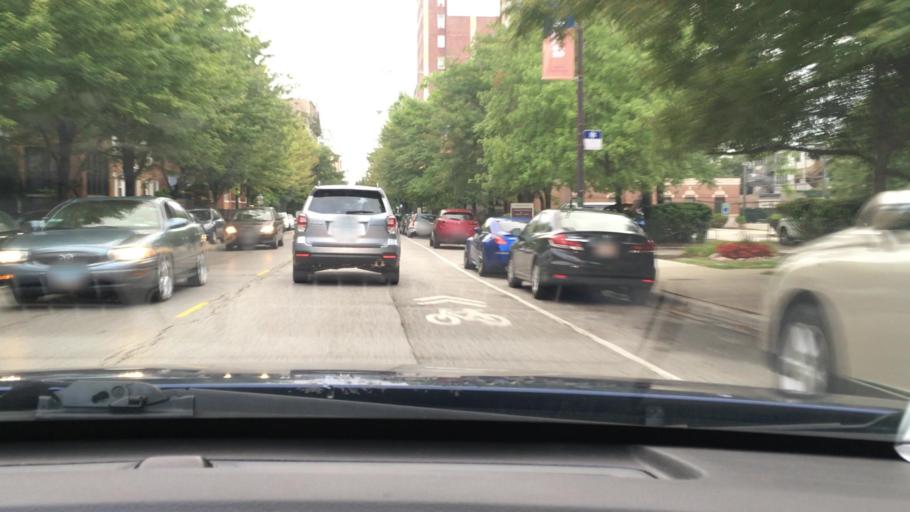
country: US
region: Illinois
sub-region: Cook County
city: Evanston
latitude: 41.9692
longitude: -87.6513
